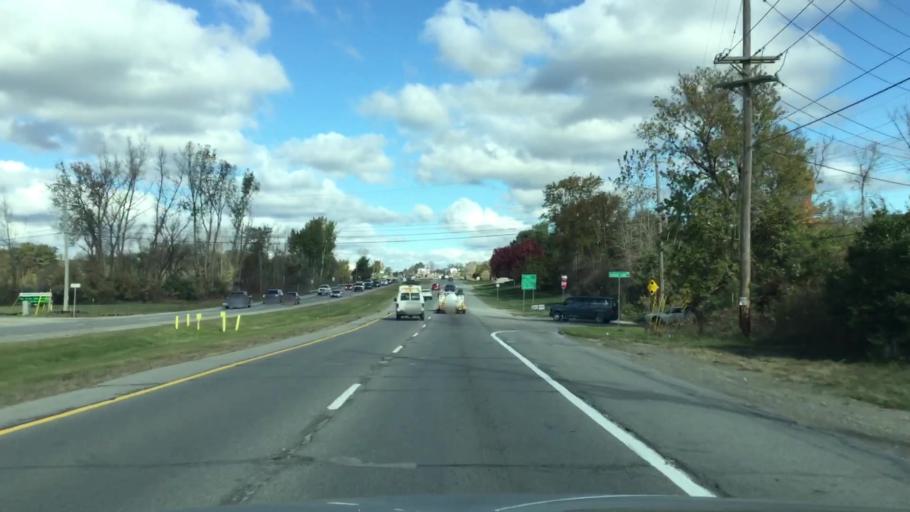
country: US
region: Michigan
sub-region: Oakland County
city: Lake Orion
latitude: 42.7968
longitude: -83.2467
